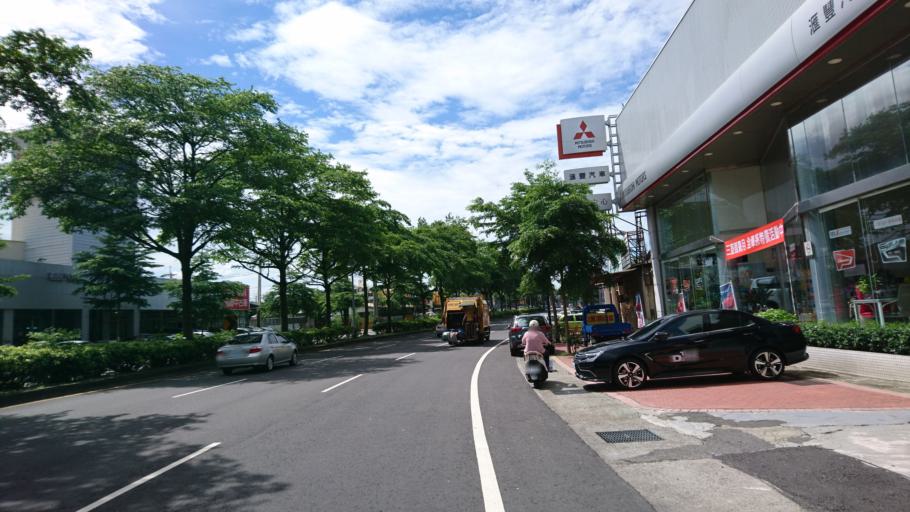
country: TW
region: Taiwan
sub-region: Taichung City
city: Taichung
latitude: 24.0982
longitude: 120.6834
